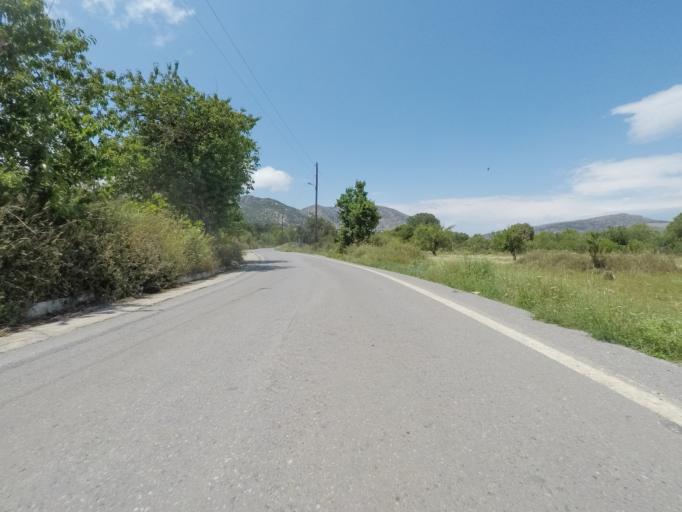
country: GR
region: Crete
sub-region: Nomos Irakleiou
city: Mokhos
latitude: 35.1678
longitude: 25.4481
